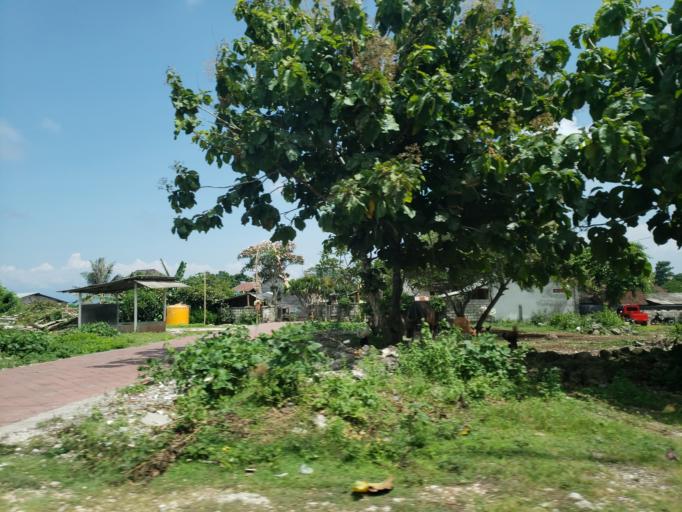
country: ID
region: Bali
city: Kangin
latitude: -8.8241
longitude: 115.1430
